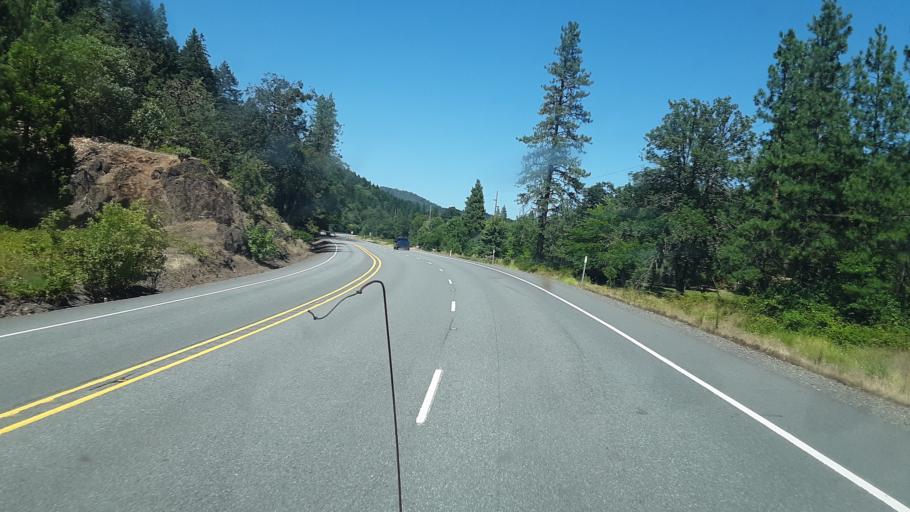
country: US
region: Oregon
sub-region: Josephine County
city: Redwood
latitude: 42.3651
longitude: -123.5098
